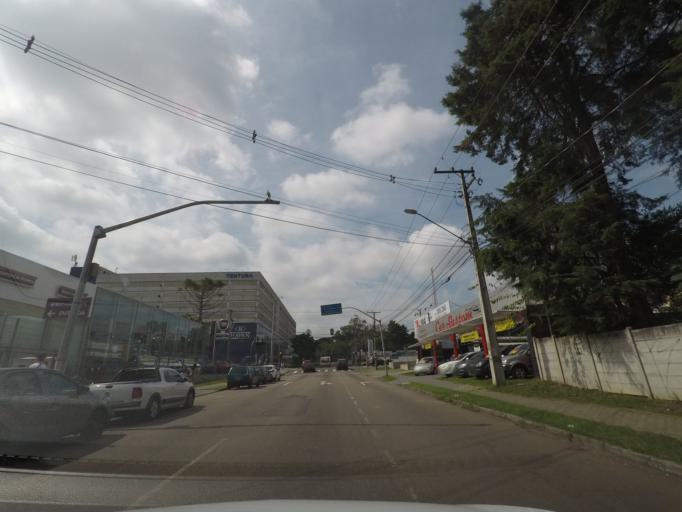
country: BR
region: Parana
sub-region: Curitiba
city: Curitiba
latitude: -25.4794
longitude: -49.2963
